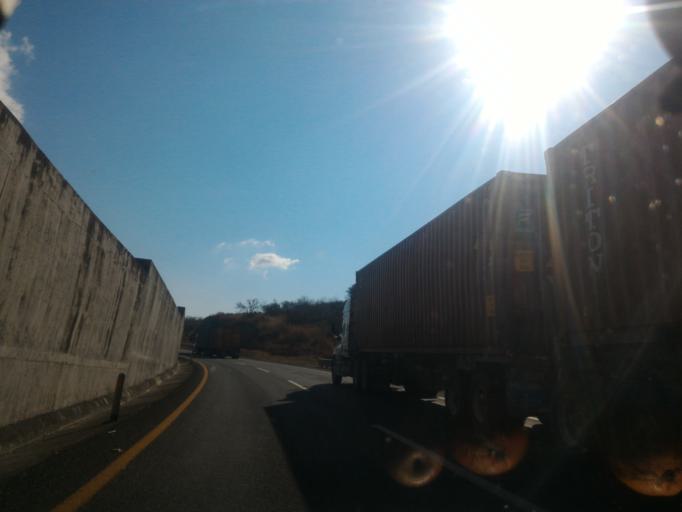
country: MX
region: Jalisco
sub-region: Tonila
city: San Marcos
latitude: 19.4324
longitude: -103.4965
